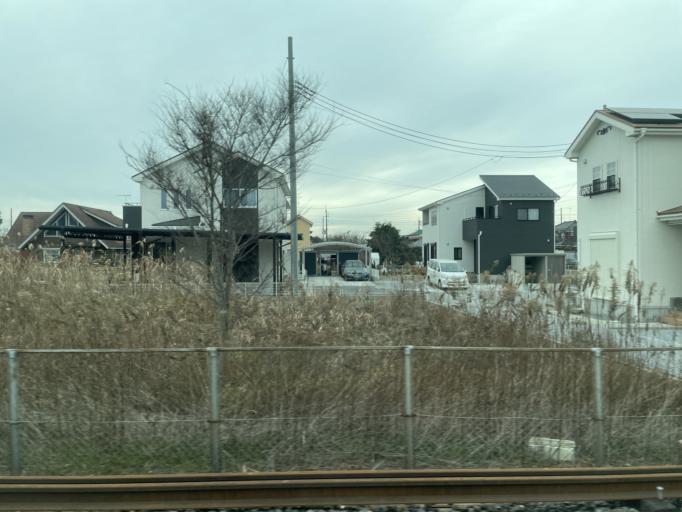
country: JP
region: Ibaraki
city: Koga
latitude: 36.1650
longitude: 139.7181
